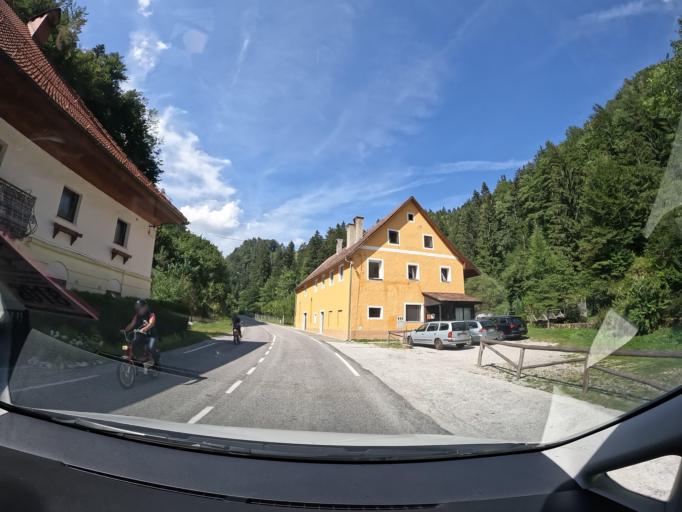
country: SI
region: Kranj
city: Golnik
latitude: 46.3822
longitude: 14.3837
